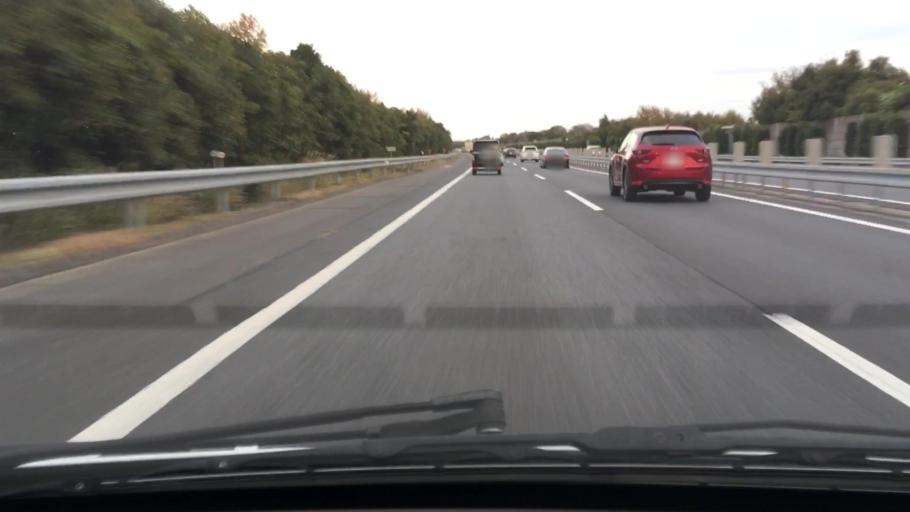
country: JP
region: Chiba
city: Ichihara
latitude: 35.5136
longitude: 140.1155
